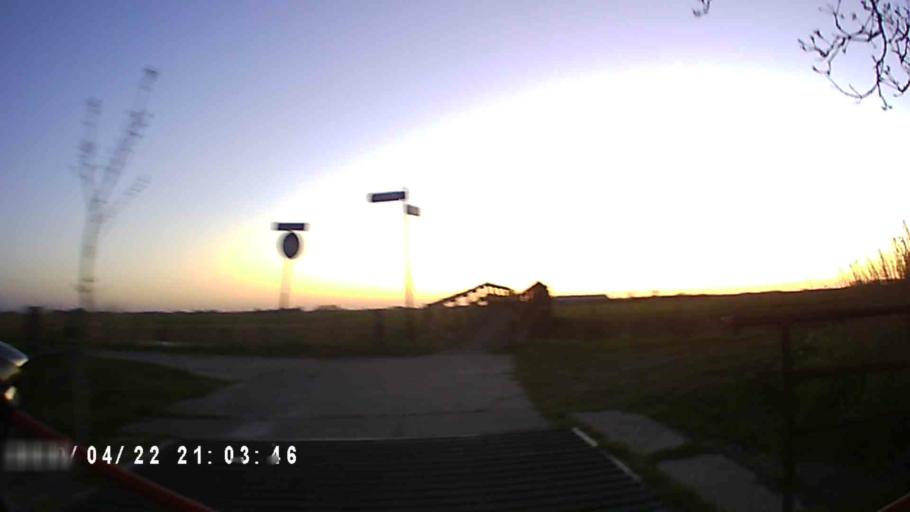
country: NL
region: Groningen
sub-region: Gemeente Winsum
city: Winsum
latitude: 53.3227
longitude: 6.5643
